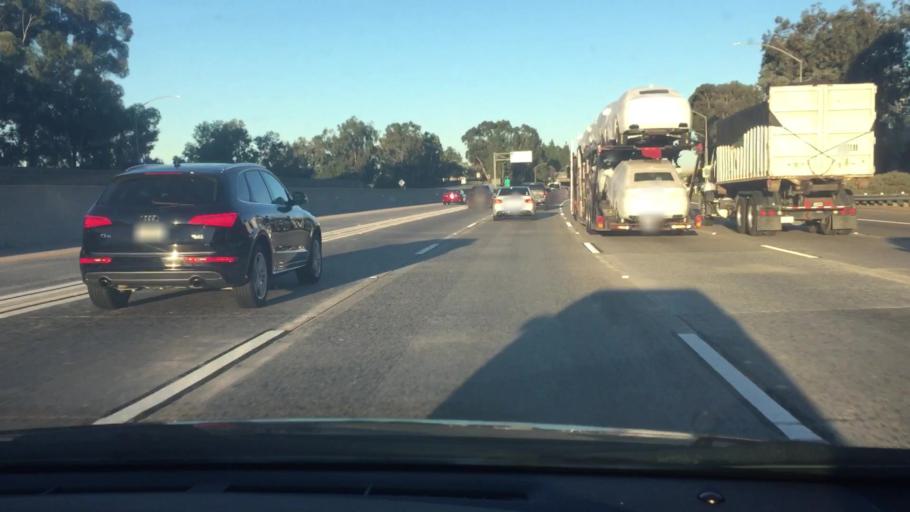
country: US
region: California
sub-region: Orange County
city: Mission Viejo
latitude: 33.6024
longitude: -117.6856
